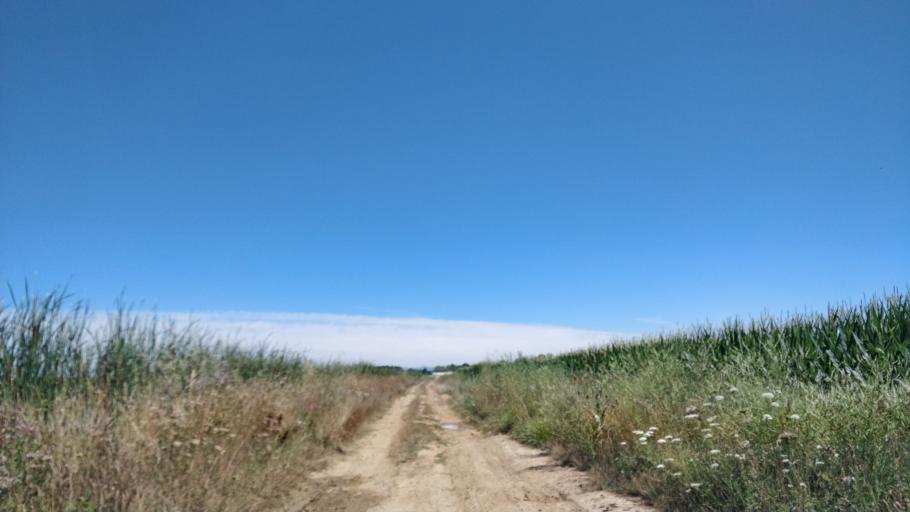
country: ES
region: Castille and Leon
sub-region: Provincia de Leon
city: Bustillo del Paramo
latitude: 42.4682
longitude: -5.8139
